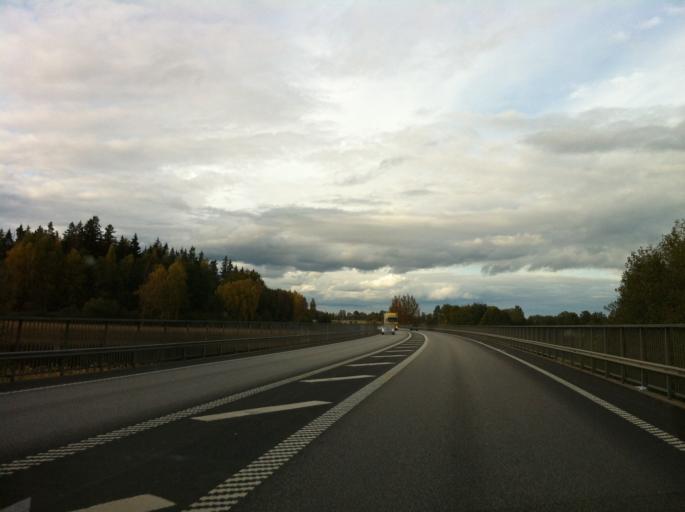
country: SE
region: OErebro
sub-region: Askersunds Kommun
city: Askersund
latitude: 58.8335
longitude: 14.9294
